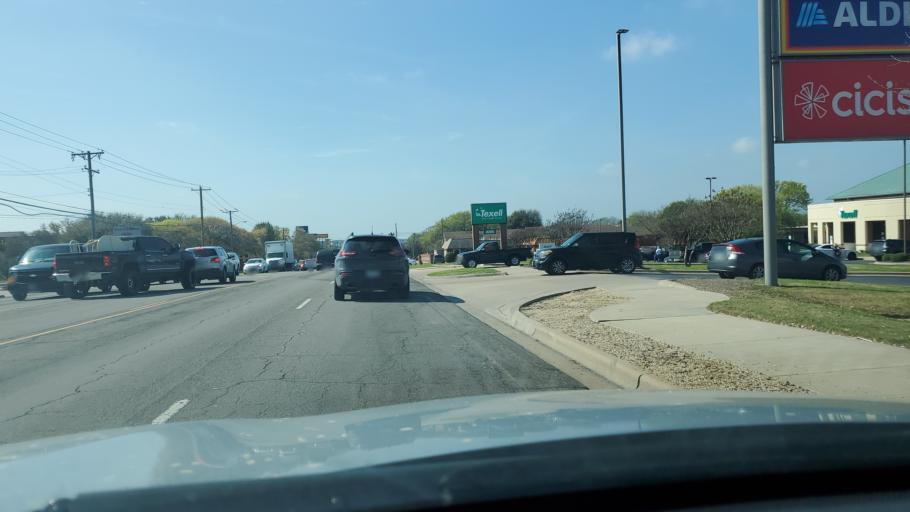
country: US
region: Texas
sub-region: Bell County
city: Temple
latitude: 31.0680
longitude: -97.3701
